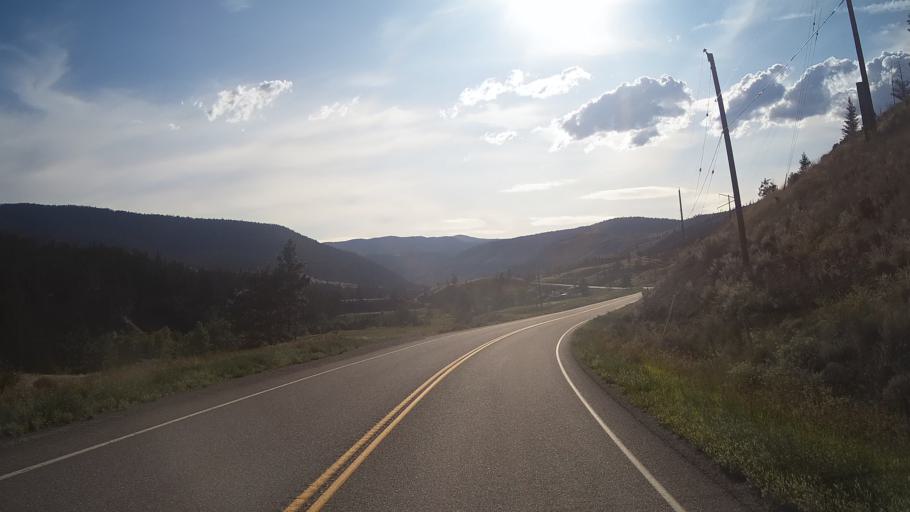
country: CA
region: British Columbia
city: Cache Creek
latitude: 50.8869
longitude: -121.4431
